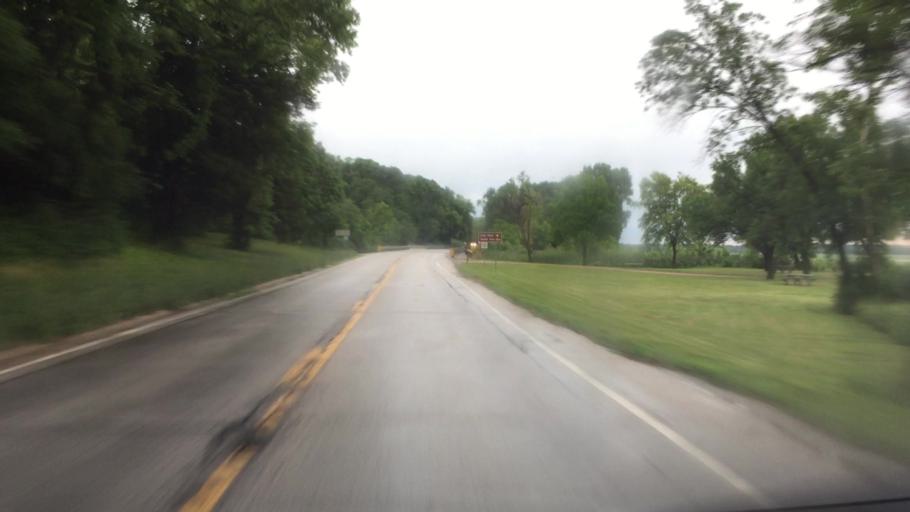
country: US
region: Iowa
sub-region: Lee County
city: Keokuk
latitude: 40.4302
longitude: -91.3678
